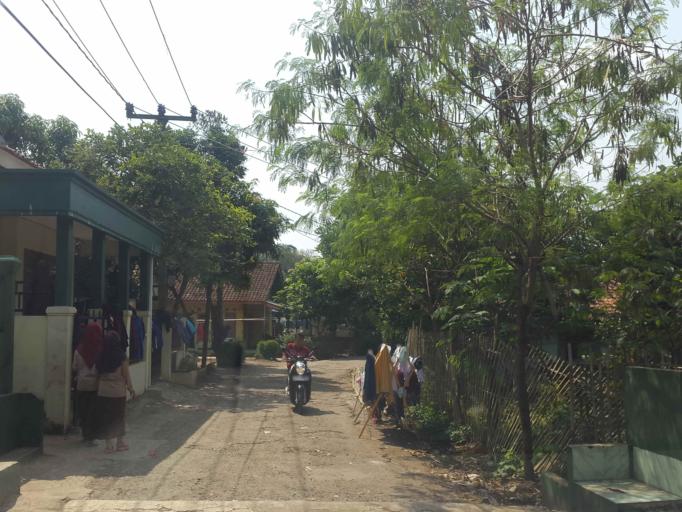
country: ID
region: West Java
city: Ciranjang-hilir
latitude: -6.7930
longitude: 107.2853
